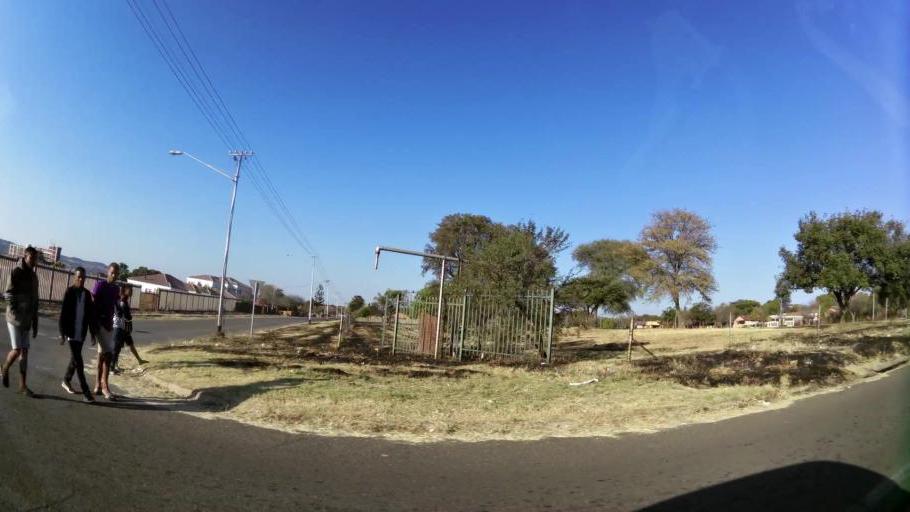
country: ZA
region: Gauteng
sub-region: City of Tshwane Metropolitan Municipality
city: Pretoria
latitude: -25.7591
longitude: 28.1150
